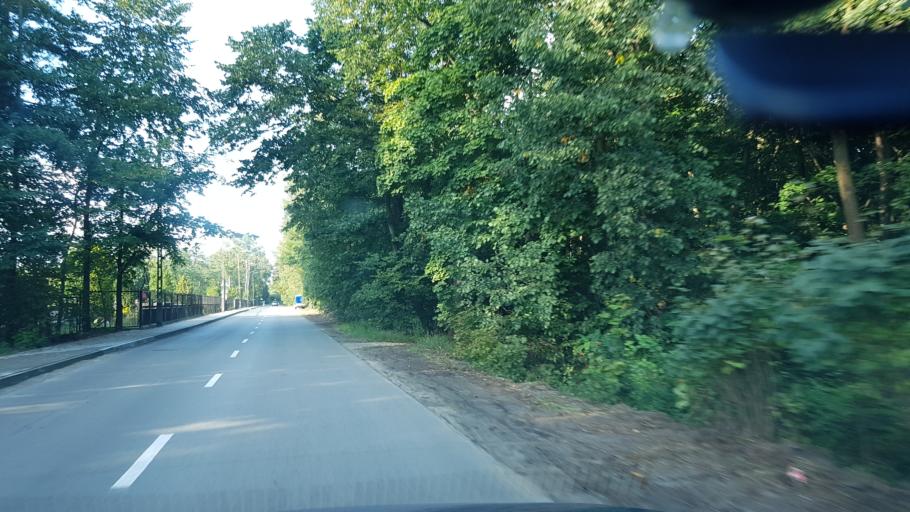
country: PL
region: Masovian Voivodeship
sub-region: Powiat piaseczynski
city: Konstancin-Jeziorna
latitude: 52.0647
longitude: 21.0989
